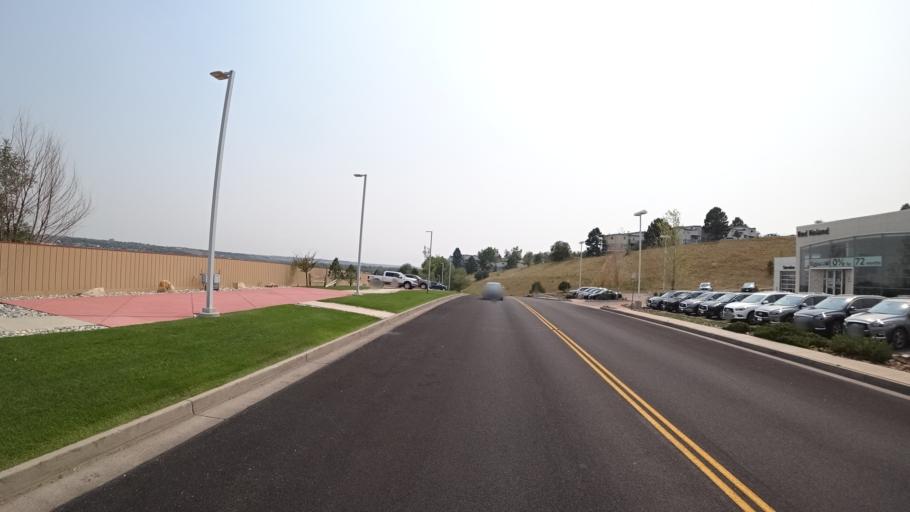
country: US
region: Colorado
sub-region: El Paso County
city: Colorado Springs
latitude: 38.8163
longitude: -104.8361
